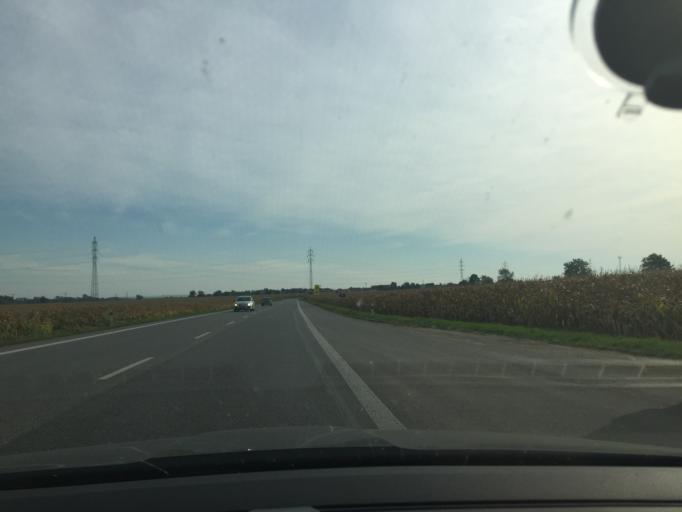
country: CZ
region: Central Bohemia
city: Cirkvice
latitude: 49.9653
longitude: 15.3137
